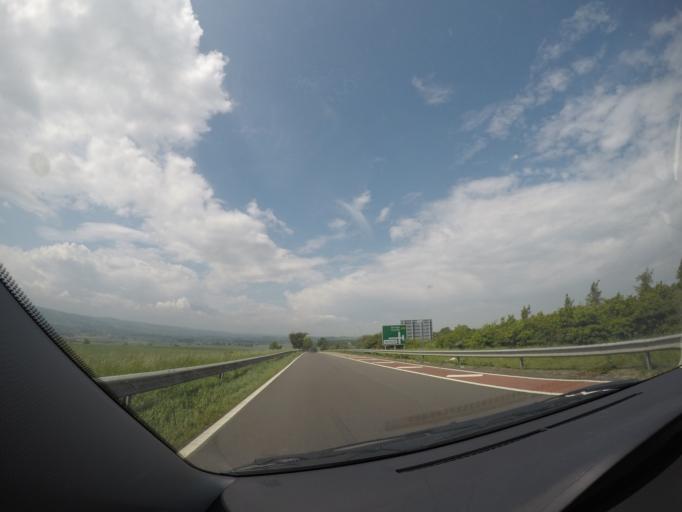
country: GB
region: England
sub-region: County Durham
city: Hutton Magna
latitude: 54.4651
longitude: -1.7389
